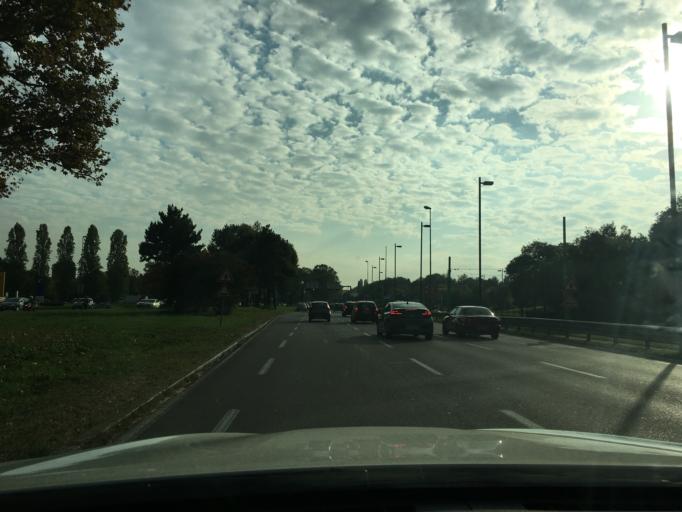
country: IT
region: Lombardy
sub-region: Citta metropolitana di Milano
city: Sesto San Giovanni
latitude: 45.5351
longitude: 9.2166
